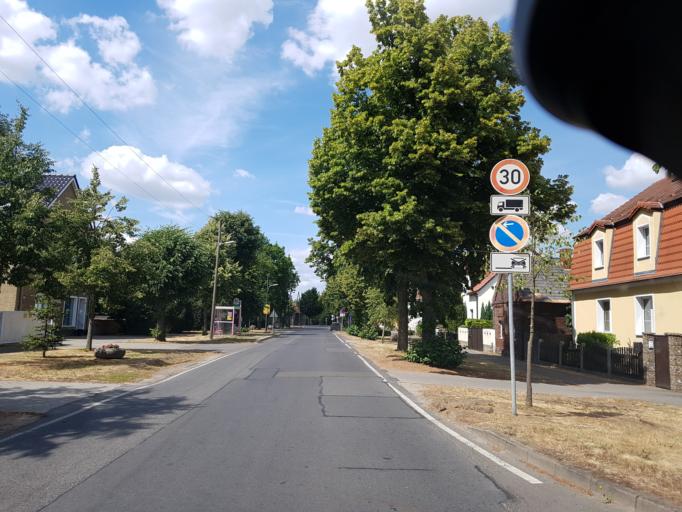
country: DE
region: Brandenburg
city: Cottbus
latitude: 51.7196
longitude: 14.4158
